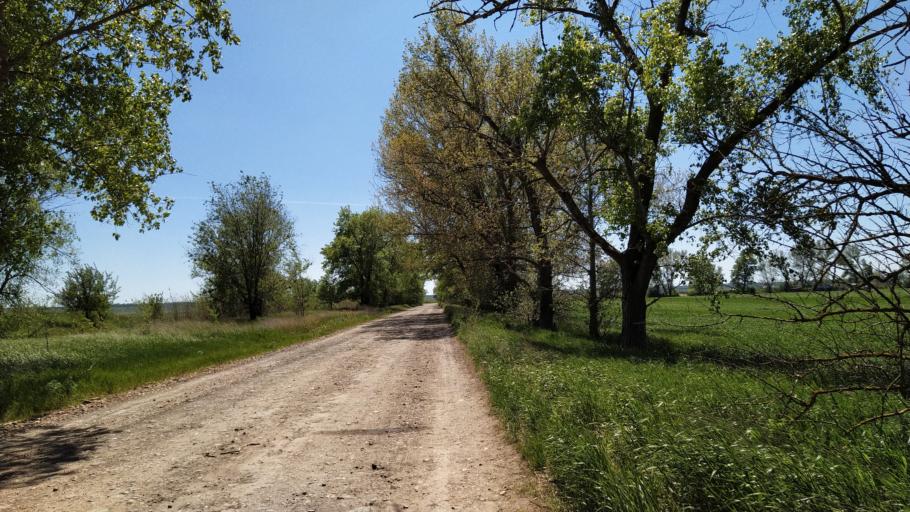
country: RU
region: Rostov
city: Kuleshovka
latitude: 47.0599
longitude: 39.6250
